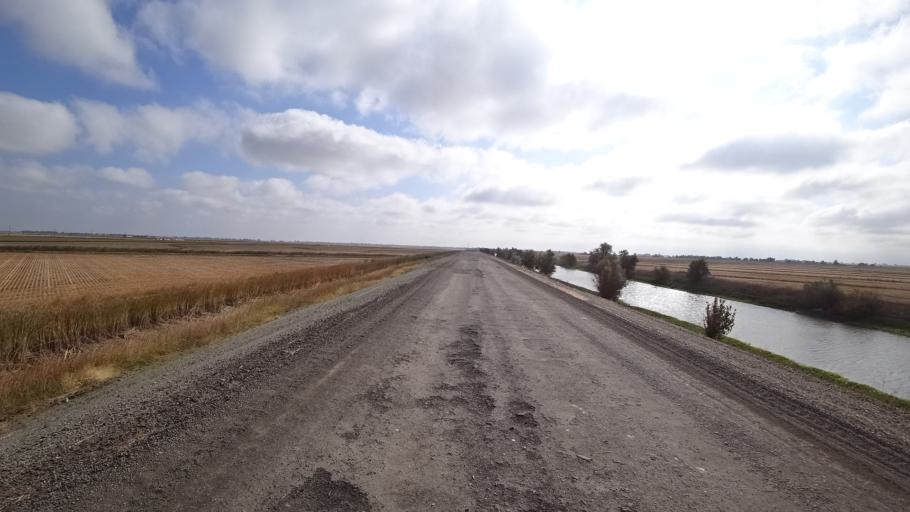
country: US
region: California
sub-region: Yolo County
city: Woodland
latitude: 38.8168
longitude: -121.7832
